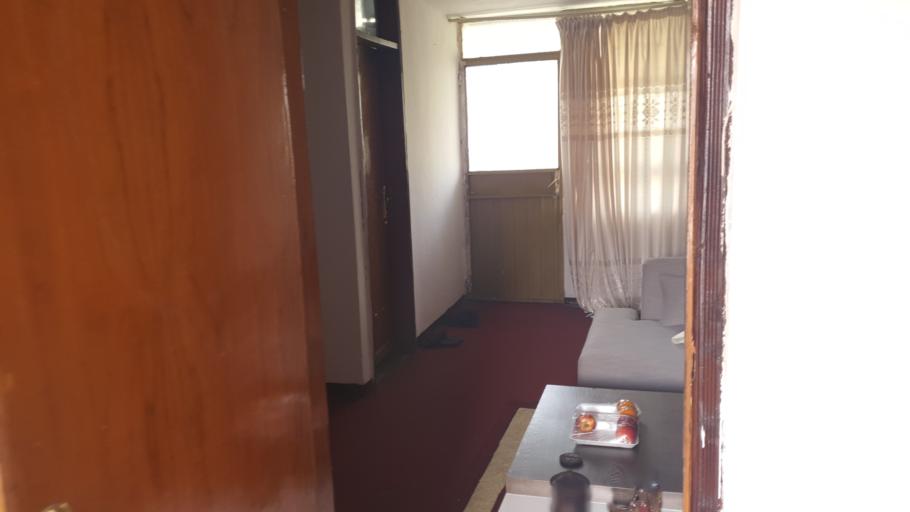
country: ET
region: Adis Abeba
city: Addis Ababa
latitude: 9.0054
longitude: 38.7964
